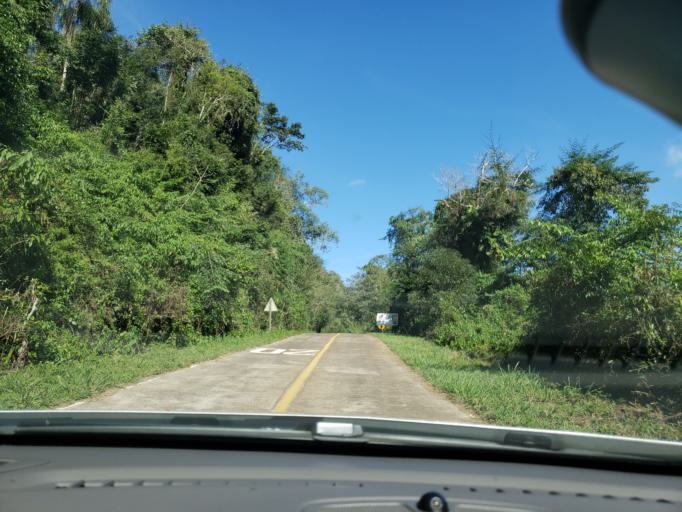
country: BR
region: Rio Grande do Sul
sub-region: Tres Passos
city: Tres Passos
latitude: -27.1459
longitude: -53.9076
